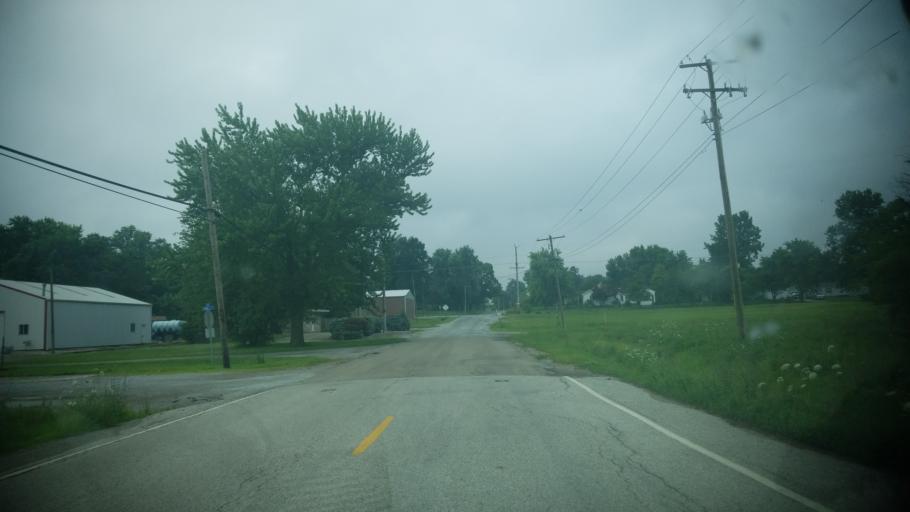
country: US
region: Illinois
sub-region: Clay County
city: Flora
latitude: 38.6793
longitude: -88.3541
